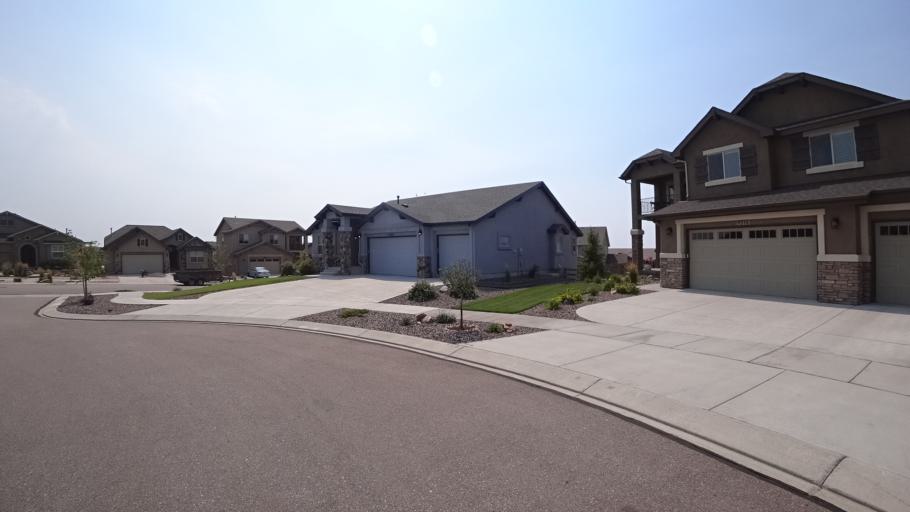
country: US
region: Colorado
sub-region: El Paso County
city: Black Forest
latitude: 38.9651
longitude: -104.7283
